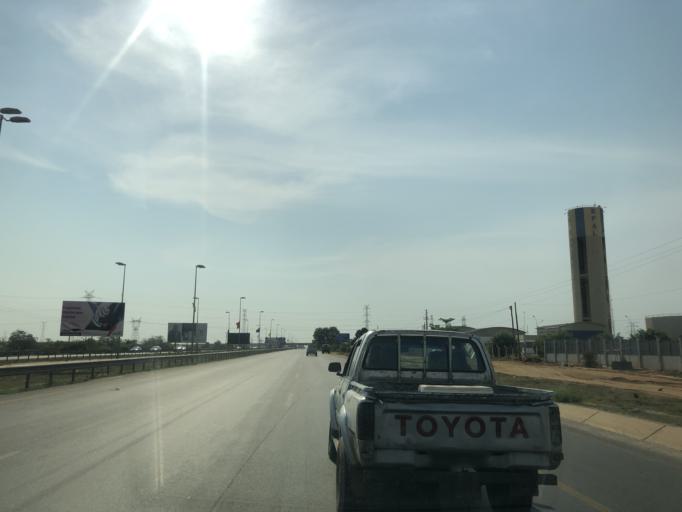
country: AO
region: Luanda
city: Luanda
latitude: -8.9732
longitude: 13.2621
